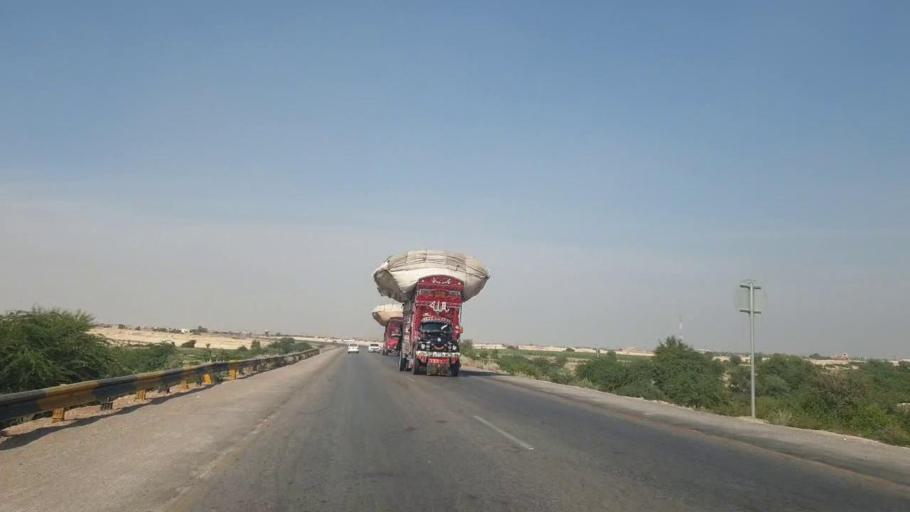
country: PK
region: Sindh
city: Hala
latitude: 25.7952
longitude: 68.2804
